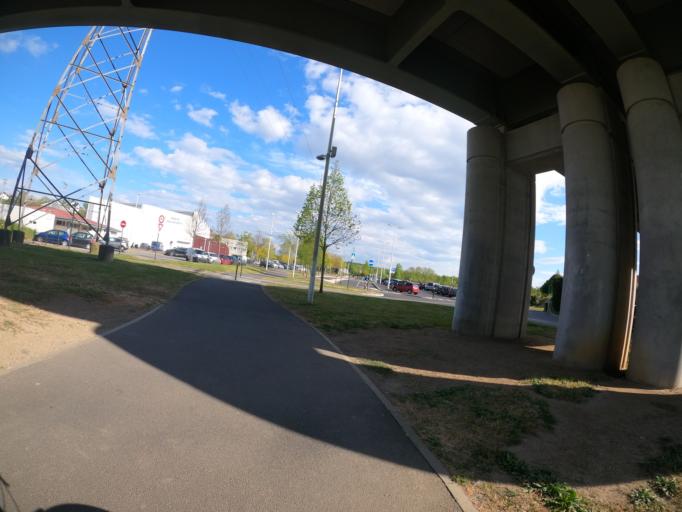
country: FR
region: Aquitaine
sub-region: Departement des Pyrenees-Atlantiques
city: Bayonne
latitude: 43.4797
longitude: -1.4744
